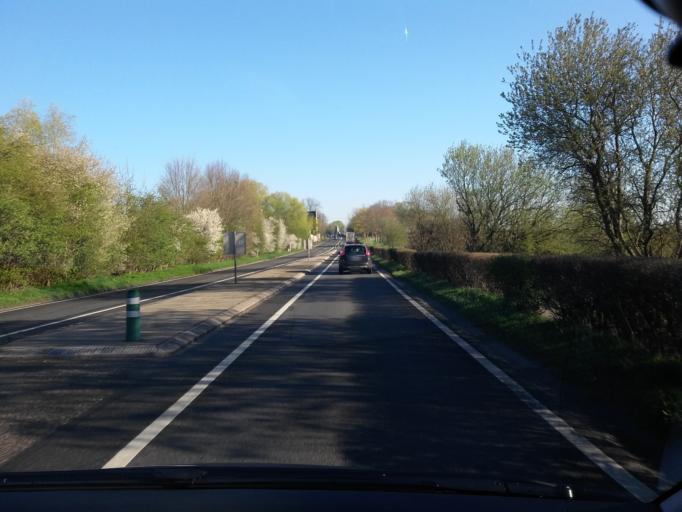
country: BE
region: Wallonia
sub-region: Province du Brabant Wallon
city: Waterloo
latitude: 50.6761
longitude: 4.4126
